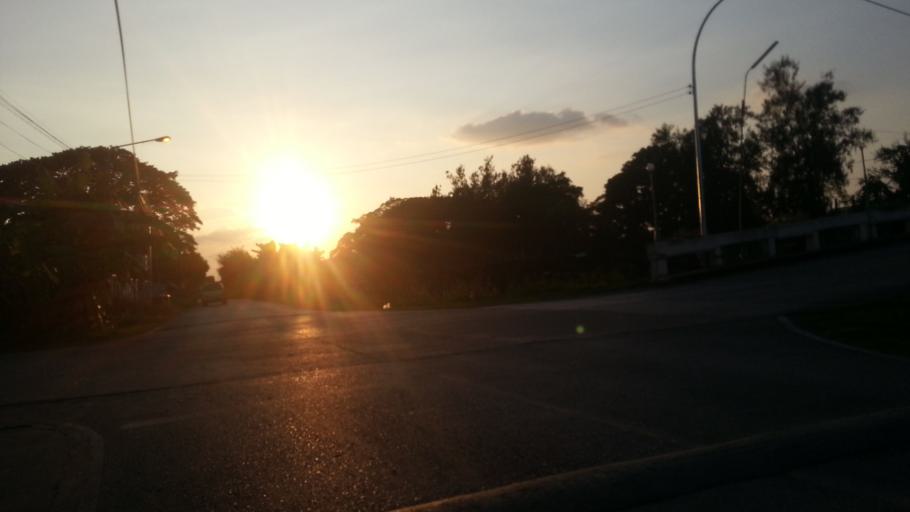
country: TH
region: Pathum Thani
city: Ban Rangsit
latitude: 14.0419
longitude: 100.7952
